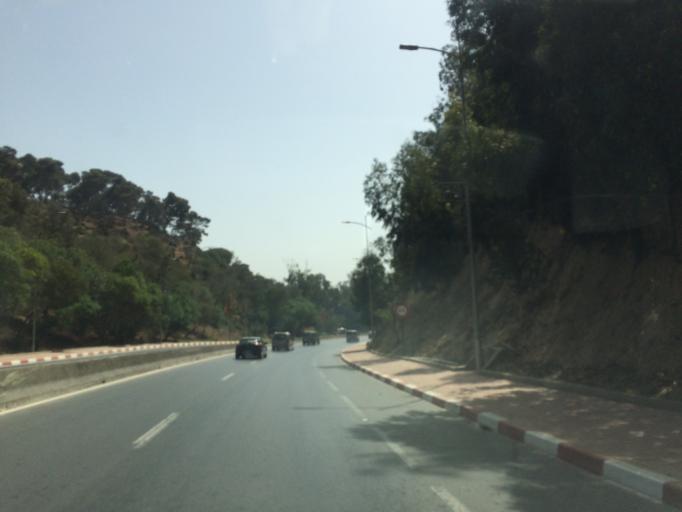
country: MA
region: Rabat-Sale-Zemmour-Zaer
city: Sale
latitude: 34.0287
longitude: -6.7951
